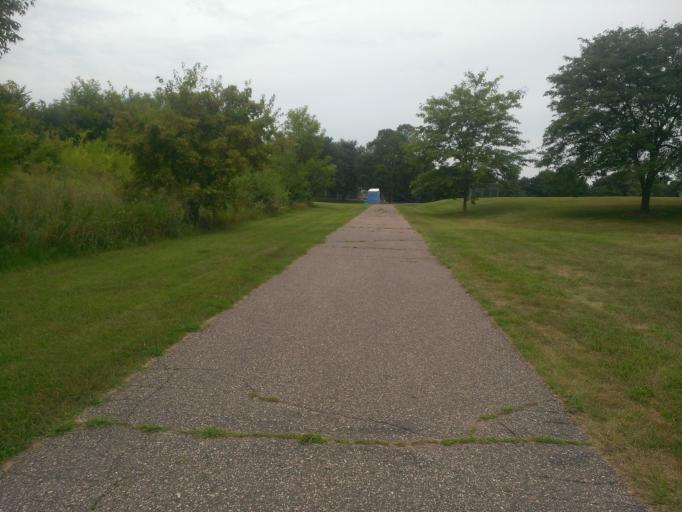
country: US
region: Minnesota
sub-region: Dakota County
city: Burnsville
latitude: 44.7546
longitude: -93.2939
